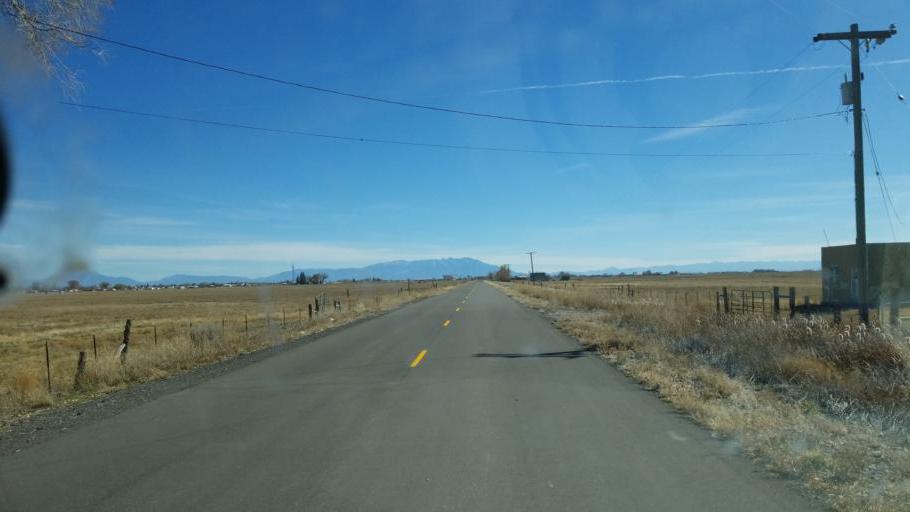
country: US
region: Colorado
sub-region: Rio Grande County
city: Monte Vista
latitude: 37.5603
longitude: -106.1648
